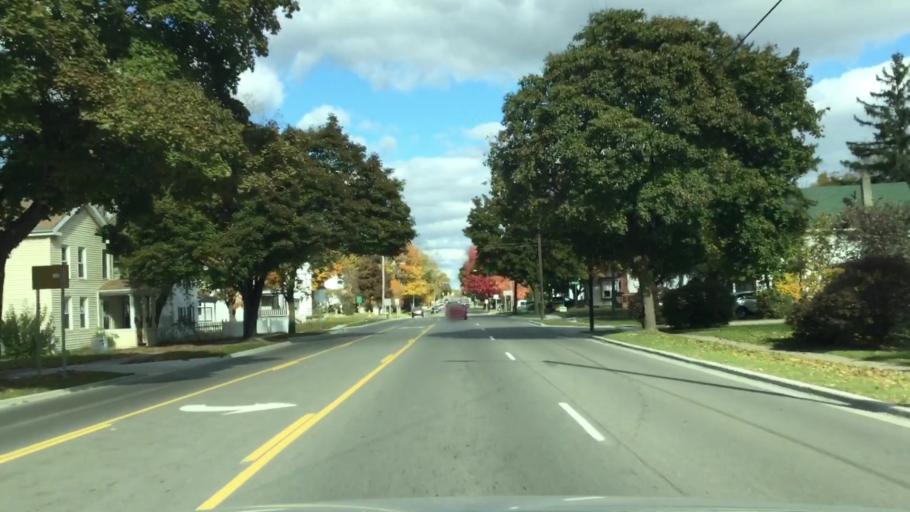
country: US
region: Michigan
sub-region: Lapeer County
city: Lapeer
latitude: 43.0534
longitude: -83.3188
